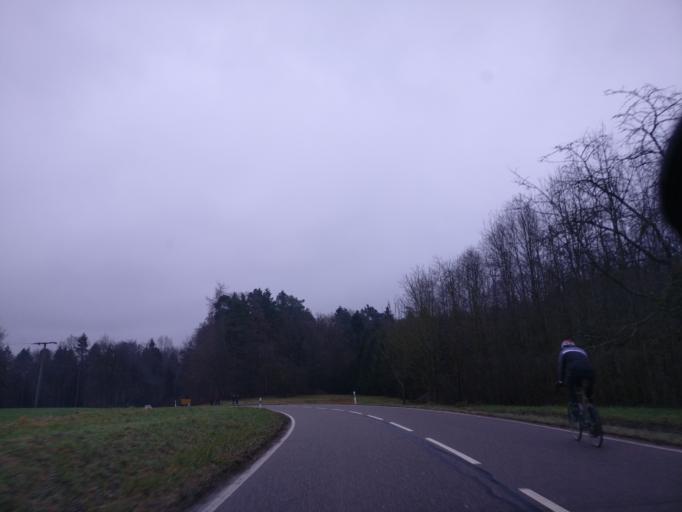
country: DE
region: Baden-Wuerttemberg
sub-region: Regierungsbezirk Stuttgart
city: Rudersberg
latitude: 48.8603
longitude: 9.4967
